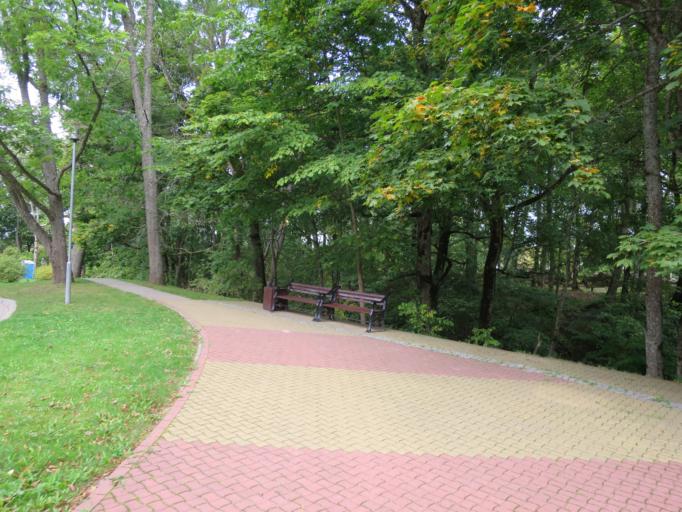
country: LV
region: Sigulda
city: Sigulda
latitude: 57.1697
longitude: 24.8314
